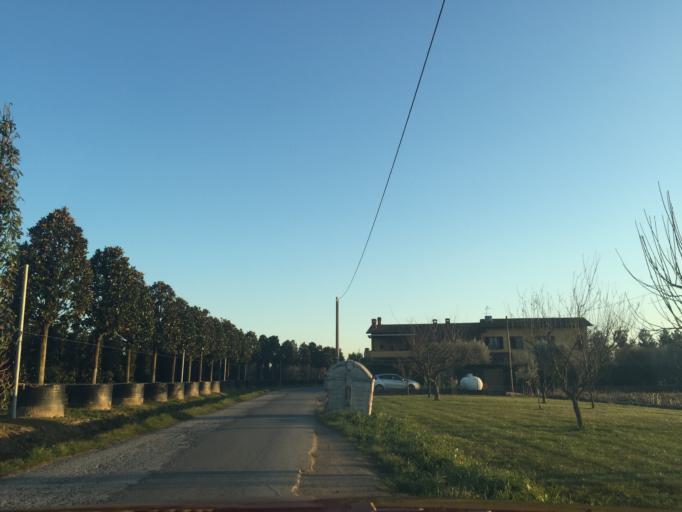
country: IT
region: Tuscany
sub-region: Provincia di Pistoia
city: Ponte Buggianese
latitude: 43.8460
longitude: 10.7557
